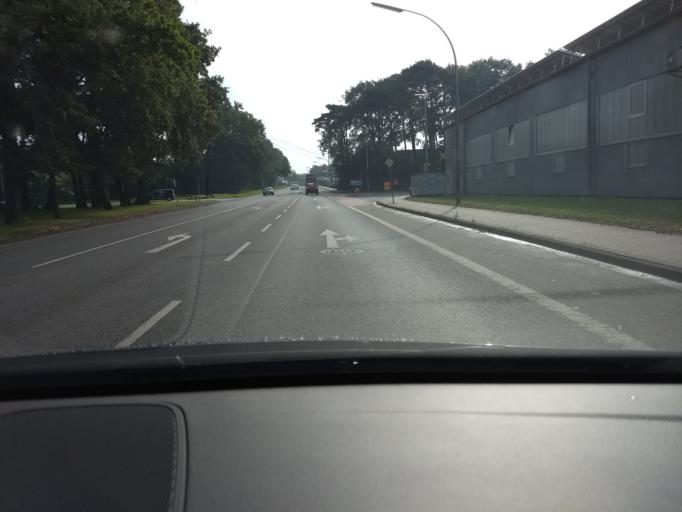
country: DE
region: North Rhine-Westphalia
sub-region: Regierungsbezirk Munster
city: Borken
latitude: 51.8527
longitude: 6.8842
